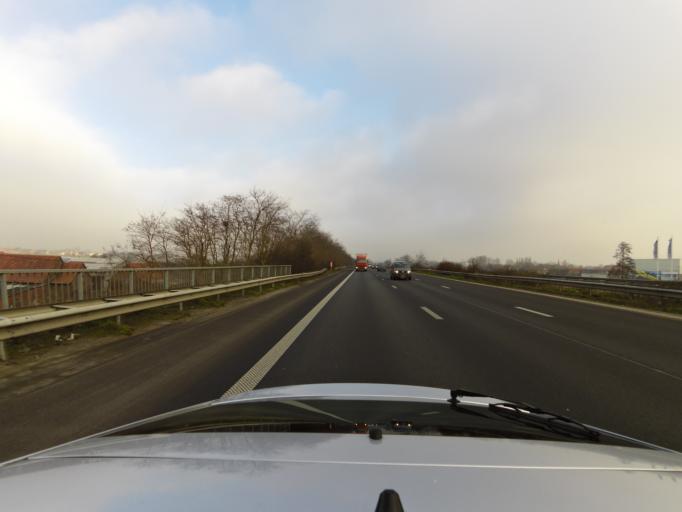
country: BE
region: Flanders
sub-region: Provincie West-Vlaanderen
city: Ledegem
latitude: 50.8729
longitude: 3.1713
